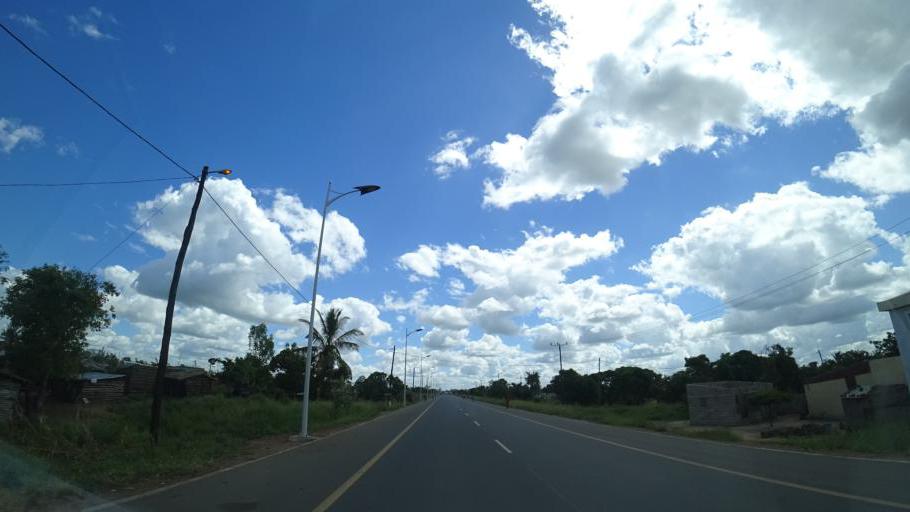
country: MZ
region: Sofala
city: Dondo
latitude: -19.2759
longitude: 34.2154
